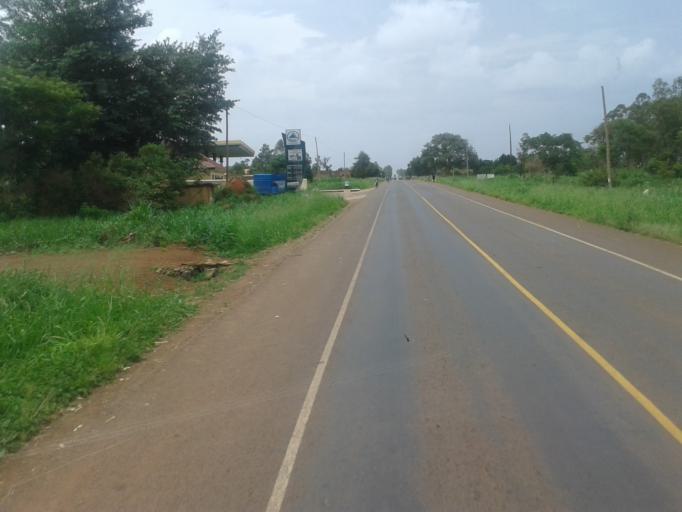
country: UG
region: Western Region
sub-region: Kiryandongo District
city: Kiryandongo
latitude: 1.9601
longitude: 32.1469
